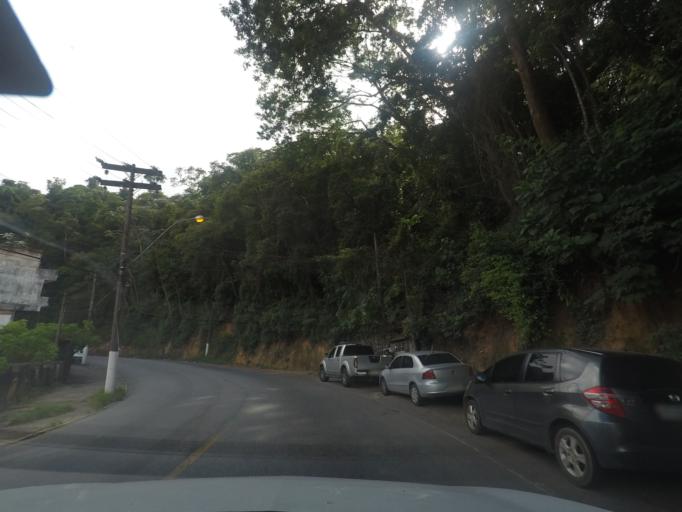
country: BR
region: Rio de Janeiro
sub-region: Teresopolis
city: Teresopolis
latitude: -22.3977
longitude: -42.9595
